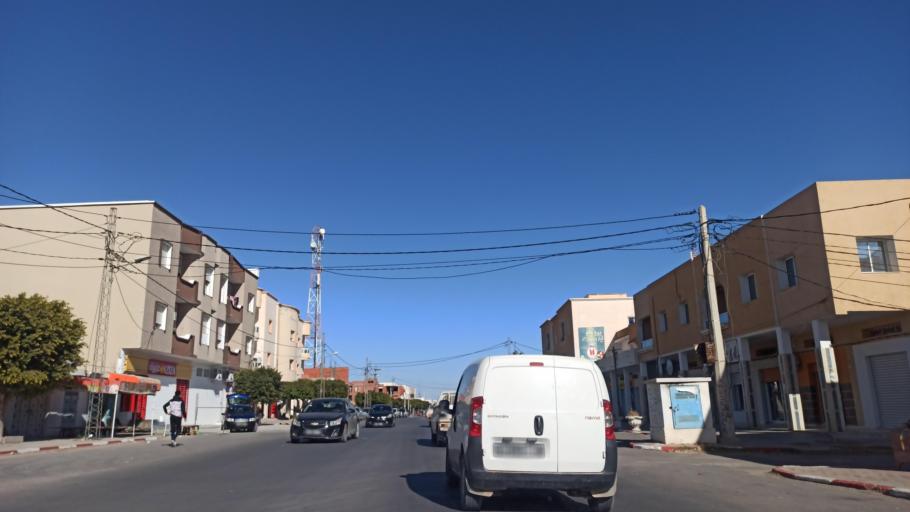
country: TN
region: Sidi Bu Zayd
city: Bi'r al Hufayy
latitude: 34.9263
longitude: 9.1913
